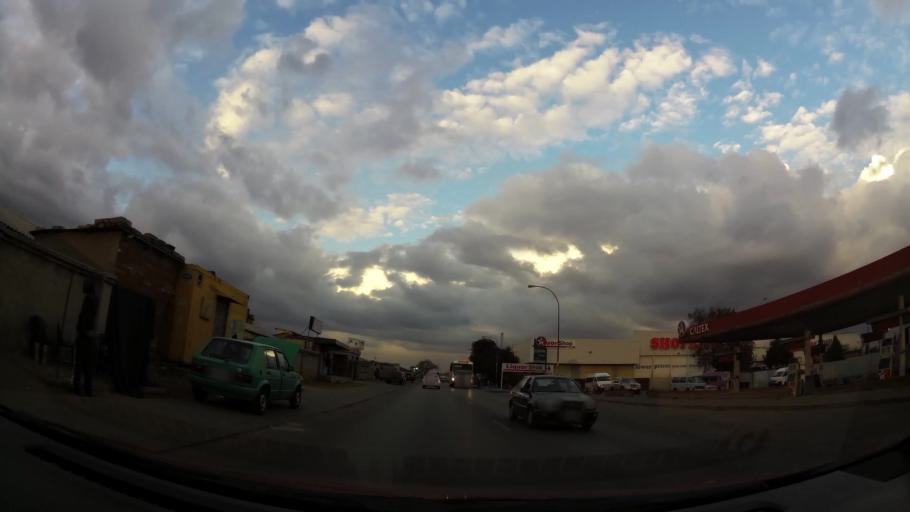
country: ZA
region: Gauteng
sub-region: City of Johannesburg Metropolitan Municipality
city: Soweto
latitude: -26.2405
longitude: 27.8460
